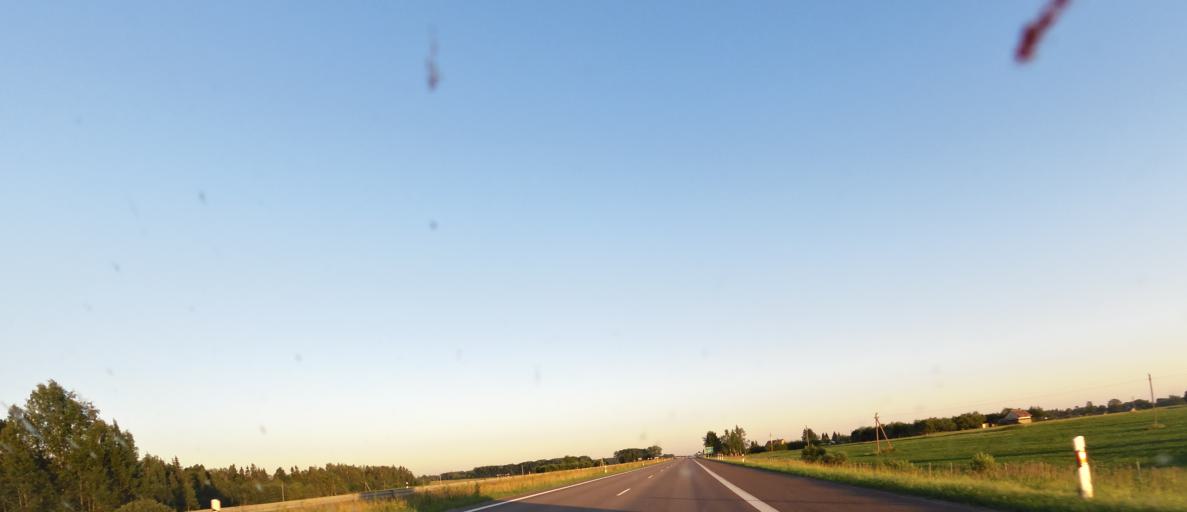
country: LT
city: Sirvintos
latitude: 55.0728
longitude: 24.8819
